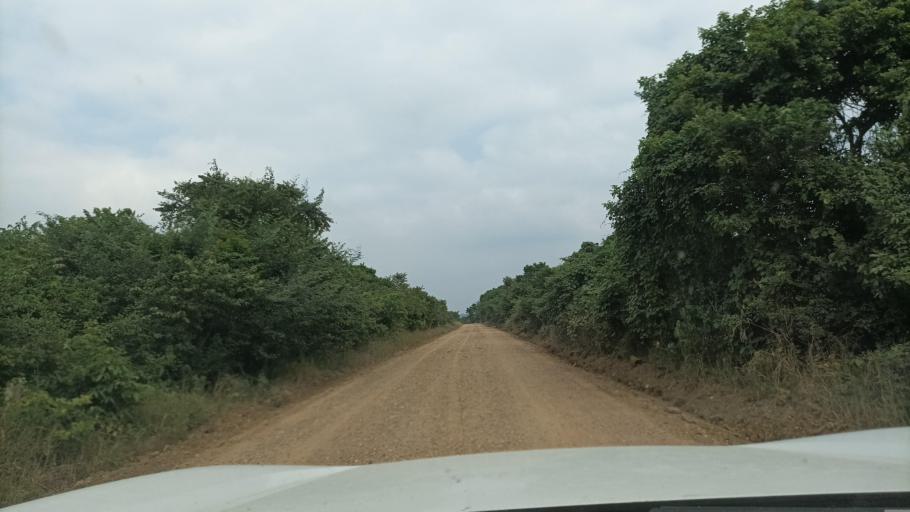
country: MX
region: Veracruz
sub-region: Texistepec
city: San Lorenzo Tenochtitlan
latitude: 17.7761
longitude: -94.7967
